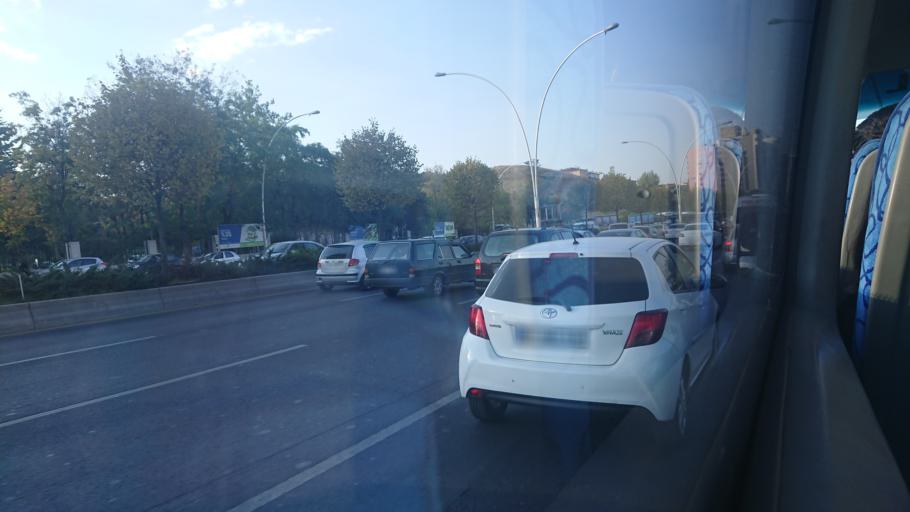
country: TR
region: Ankara
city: Ankara
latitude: 39.9211
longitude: 32.8143
